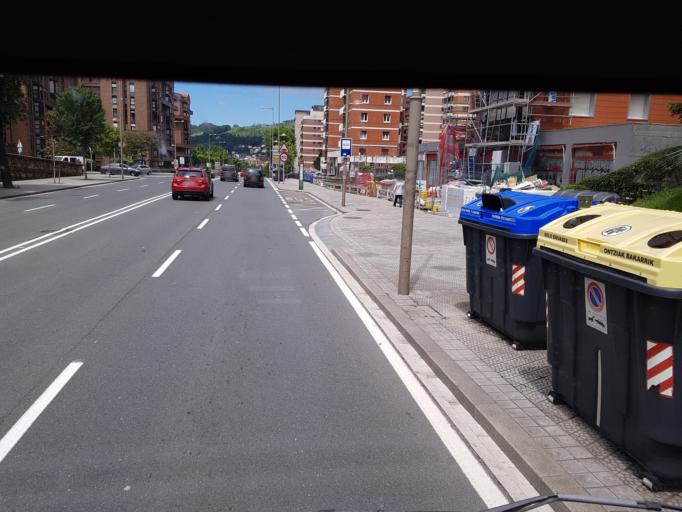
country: ES
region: Basque Country
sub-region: Bizkaia
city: Santutxu
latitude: 43.2600
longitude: -2.9138
